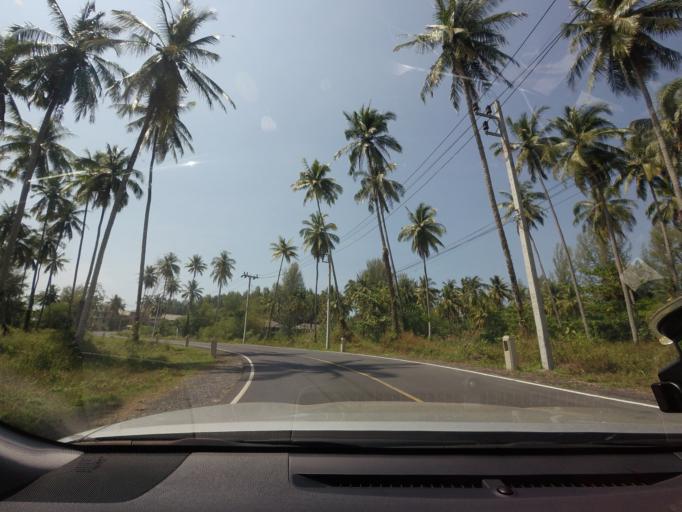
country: TH
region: Phangnga
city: Ban Khao Lak
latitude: 8.6945
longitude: 98.2433
